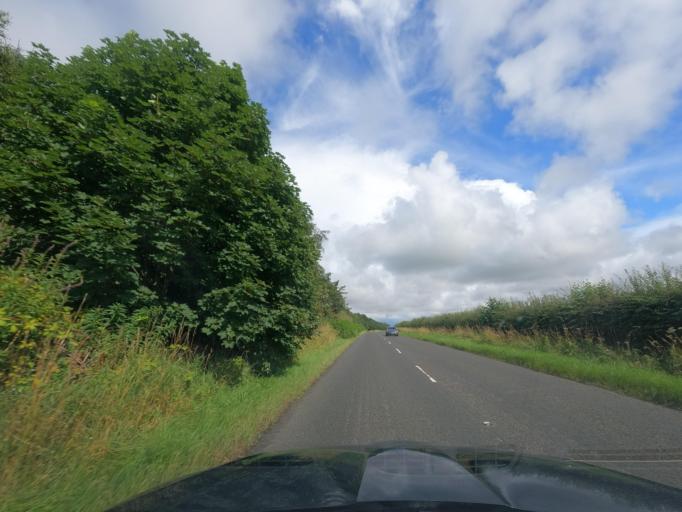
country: GB
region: England
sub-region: Northumberland
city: Doddington
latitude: 55.6051
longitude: -2.0012
